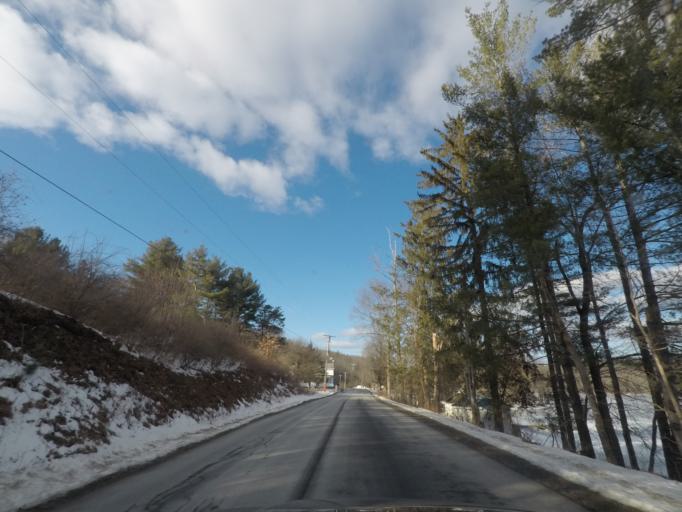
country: US
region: New York
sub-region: Rensselaer County
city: Nassau
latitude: 42.5287
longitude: -73.5288
